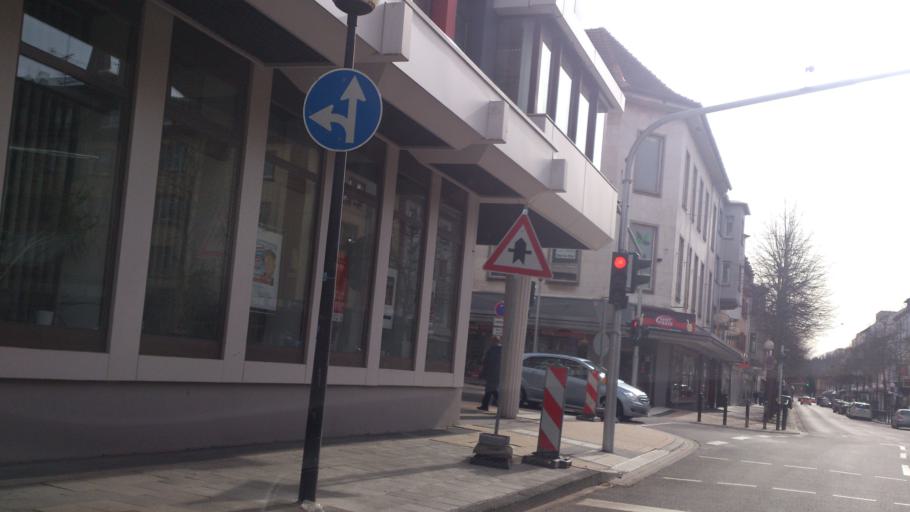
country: DE
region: Rheinland-Pfalz
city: Zweibrucken
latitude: 49.2475
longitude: 7.3659
